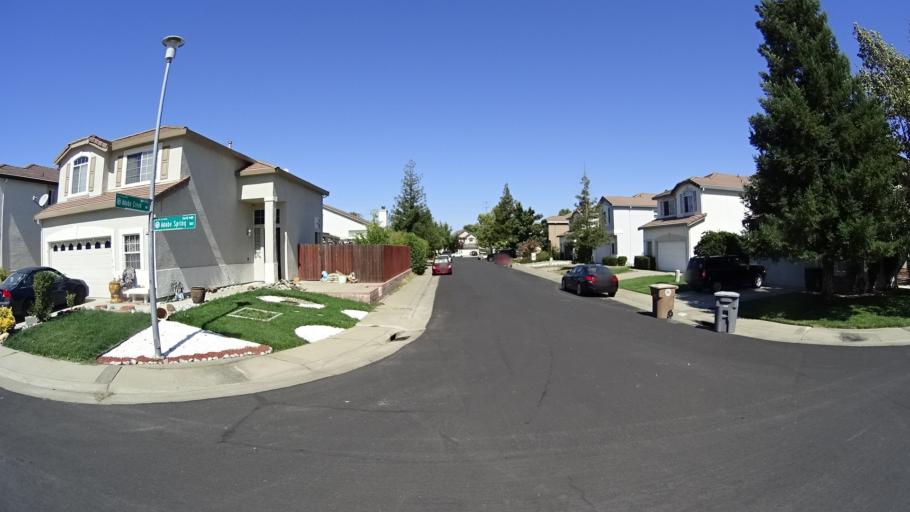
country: US
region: California
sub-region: Sacramento County
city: Laguna
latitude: 38.4315
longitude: -121.4375
